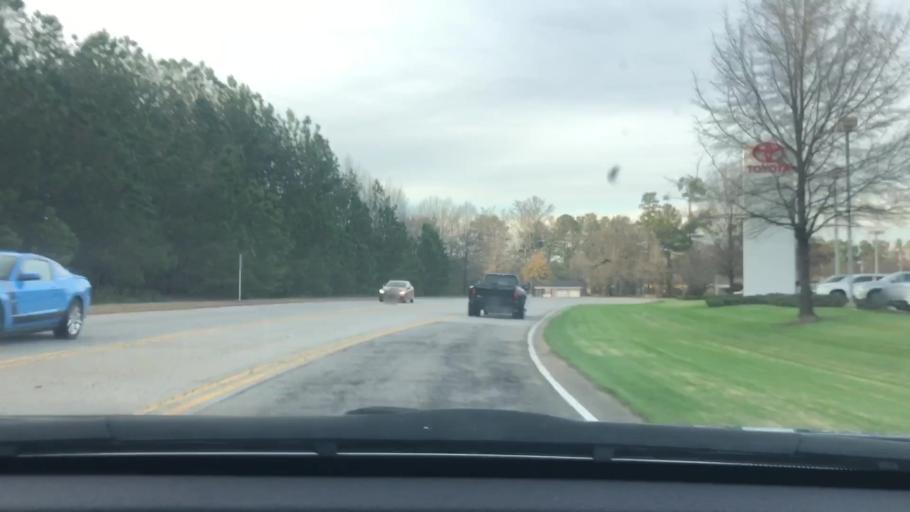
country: US
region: South Carolina
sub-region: Lexington County
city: Irmo
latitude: 34.0976
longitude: -81.1781
